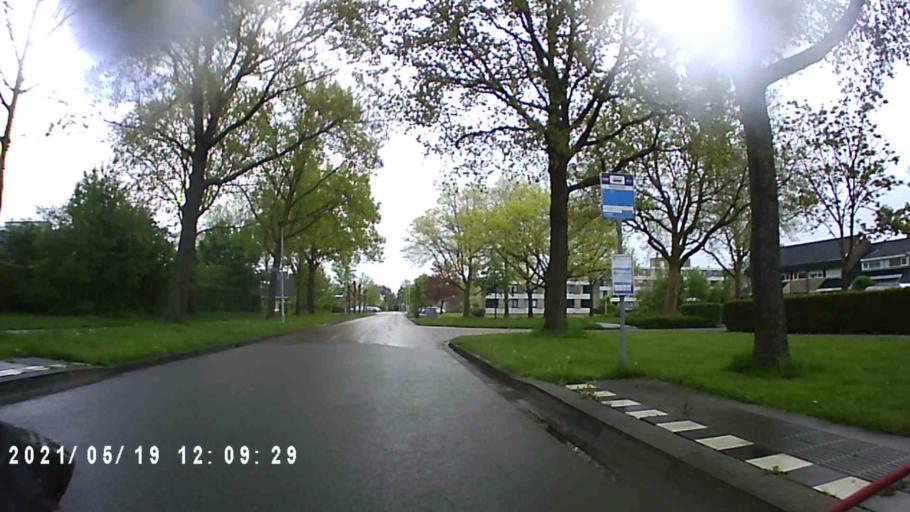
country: NL
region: Friesland
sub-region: Gemeente Achtkarspelen
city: Buitenpost
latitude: 53.2493
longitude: 6.1398
